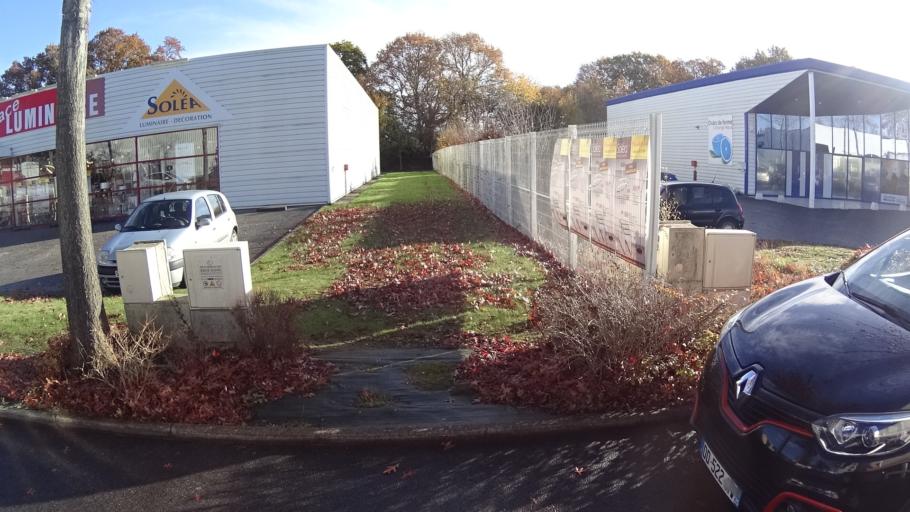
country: FR
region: Pays de la Loire
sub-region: Departement de la Loire-Atlantique
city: Saint-Nicolas-de-Redon
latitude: 47.6703
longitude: -2.0655
